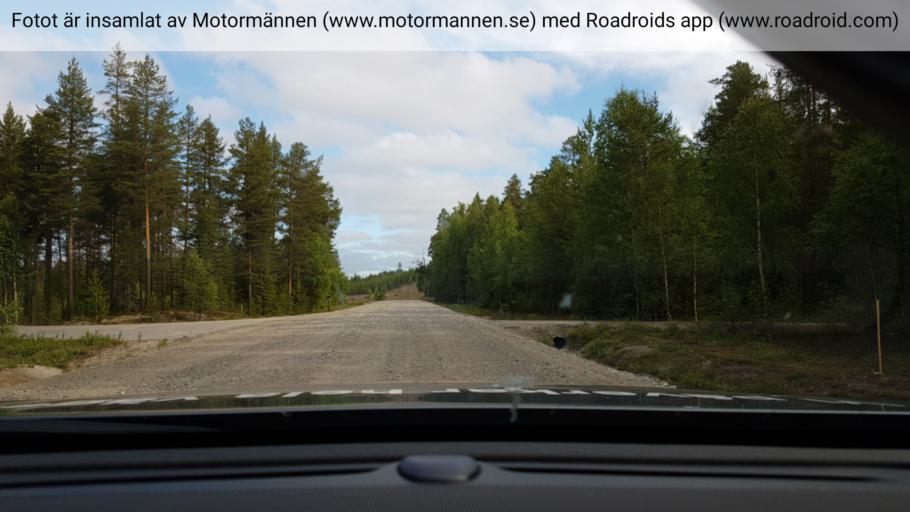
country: SE
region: Vaesterbotten
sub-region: Norsjo Kommun
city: Norsjoe
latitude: 64.6174
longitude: 19.2892
